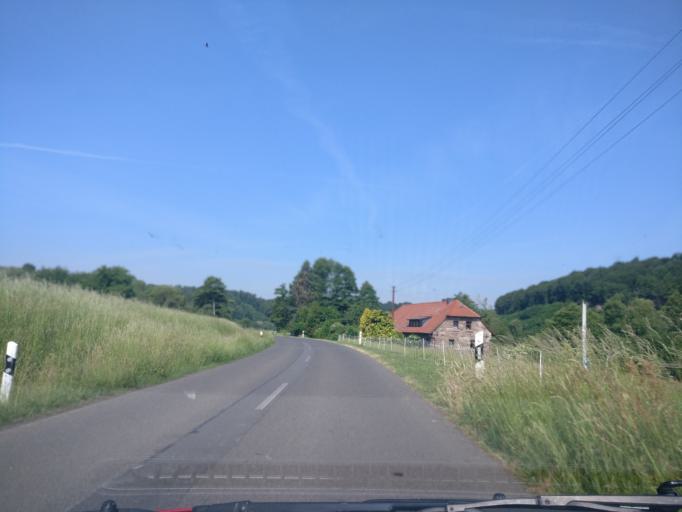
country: DE
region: Lower Saxony
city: Scheden
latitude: 51.3905
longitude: 9.7390
